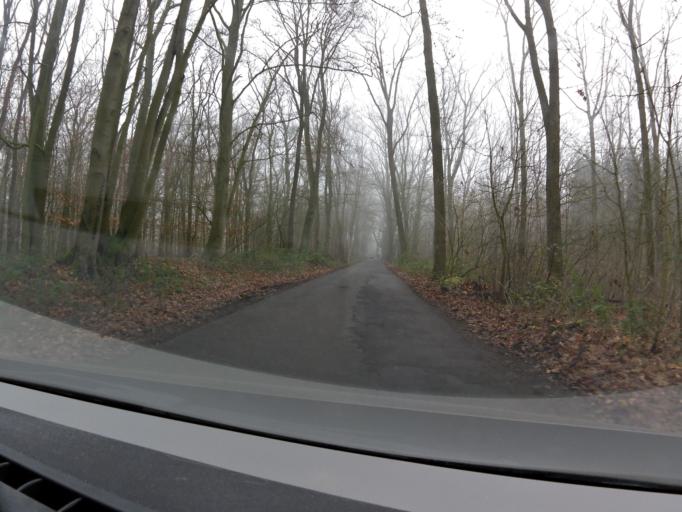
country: DE
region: North Rhine-Westphalia
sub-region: Regierungsbezirk Dusseldorf
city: Nettetal
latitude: 51.3439
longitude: 6.2574
